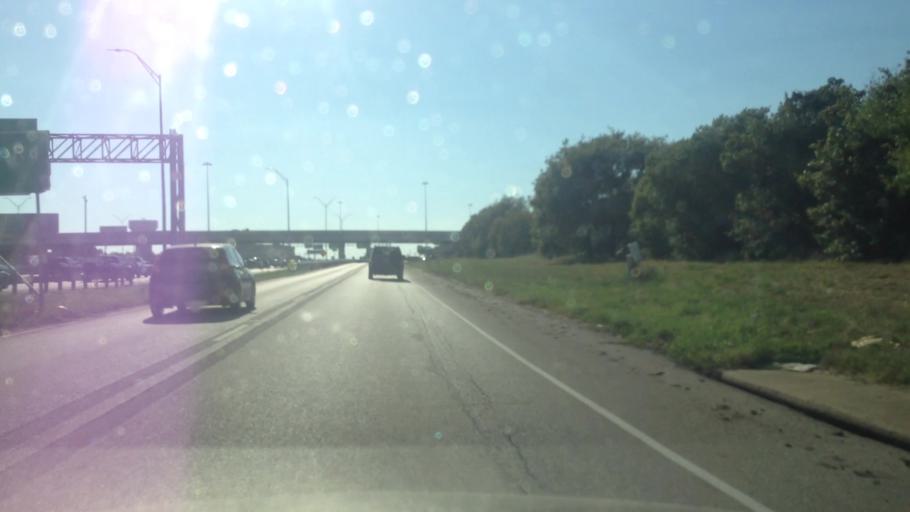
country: US
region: Texas
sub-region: Tarrant County
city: Euless
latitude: 32.8375
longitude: -97.0670
